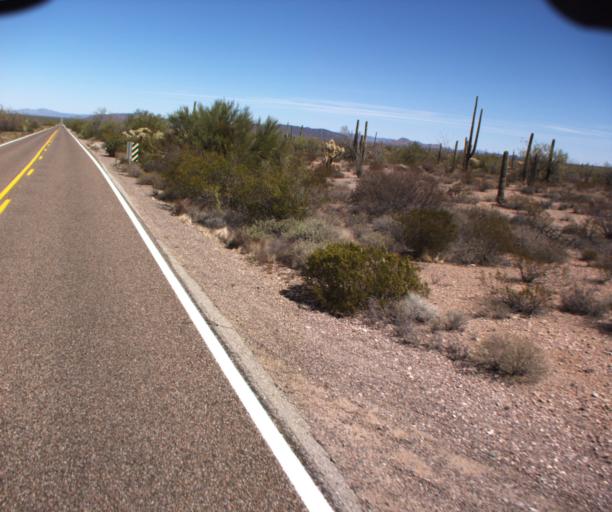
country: MX
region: Sonora
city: Sonoyta
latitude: 32.1018
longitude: -112.7710
